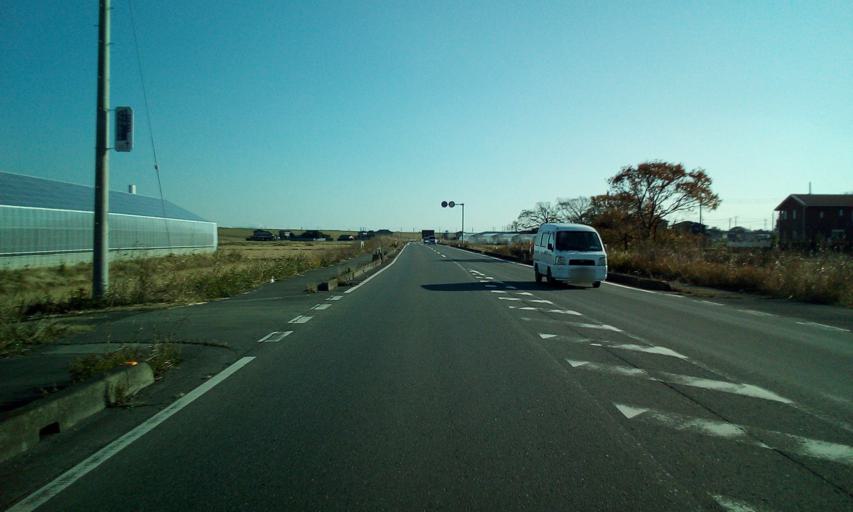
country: JP
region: Chiba
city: Nagareyama
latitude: 35.8868
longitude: 139.8847
